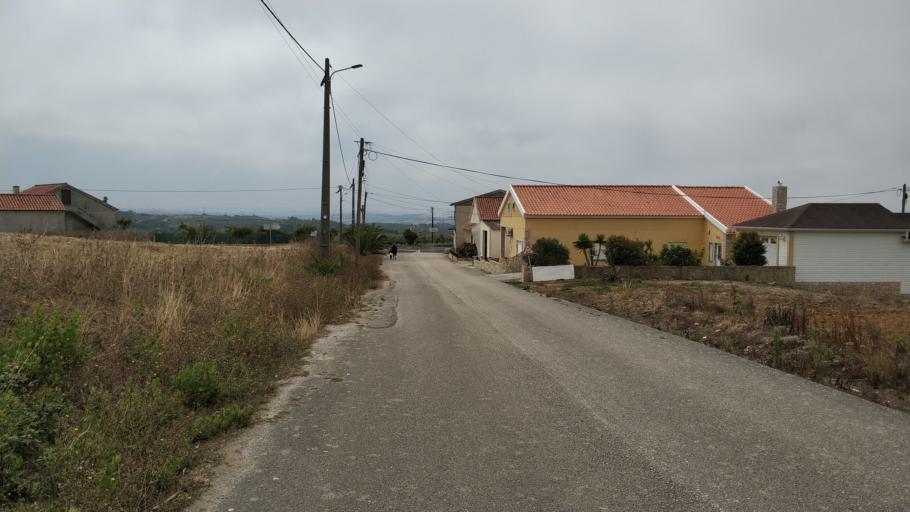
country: PT
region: Lisbon
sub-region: Lourinha
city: Lourinha
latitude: 39.2104
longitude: -9.3211
